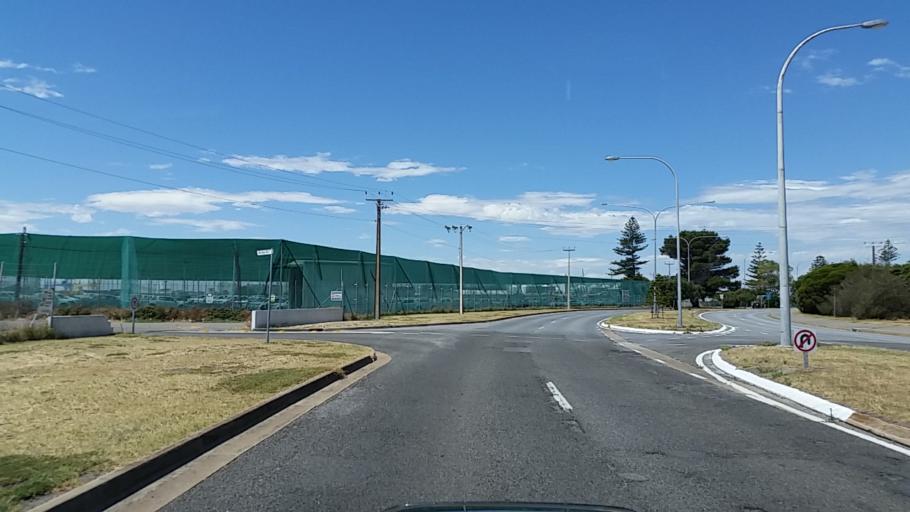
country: AU
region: South Australia
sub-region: Port Adelaide Enfield
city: Birkenhead
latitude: -34.7764
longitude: 138.4855
